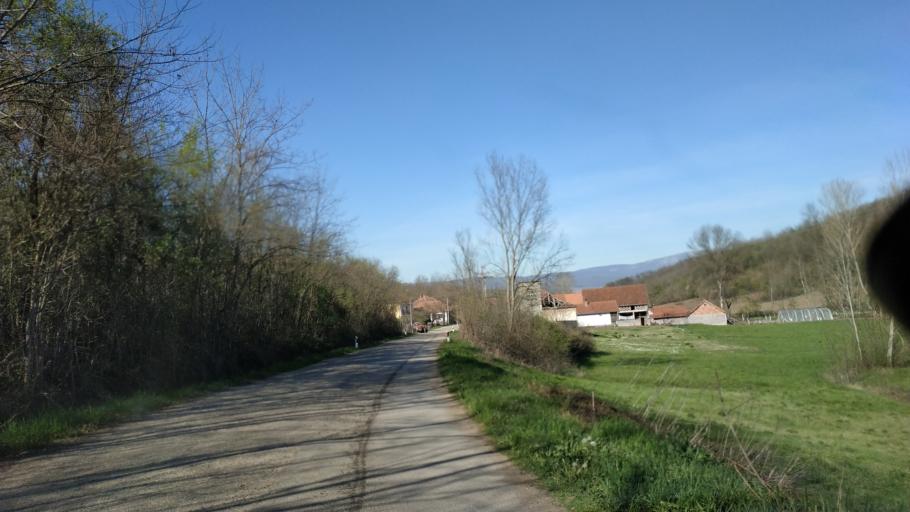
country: RS
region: Central Serbia
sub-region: Nisavski Okrug
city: Aleksinac
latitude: 43.4791
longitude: 21.6522
